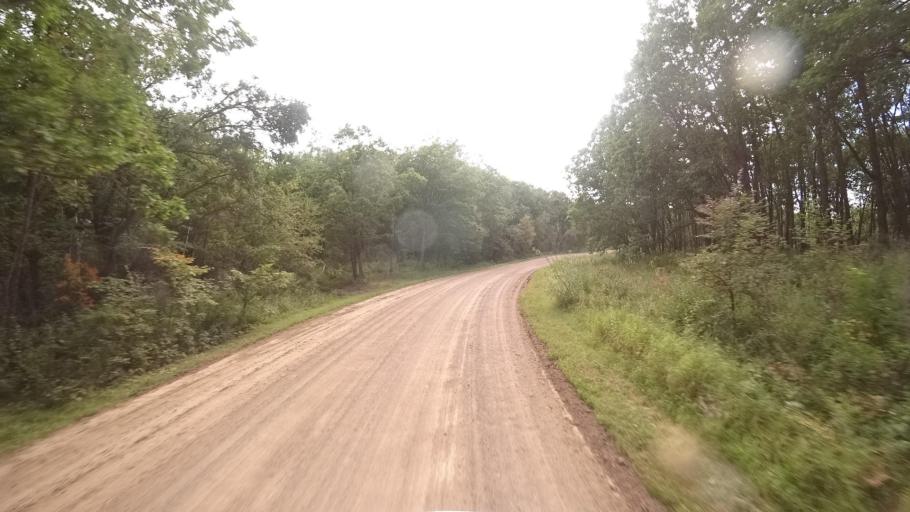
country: RU
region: Primorskiy
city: Dostoyevka
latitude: 44.3482
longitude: 133.5191
